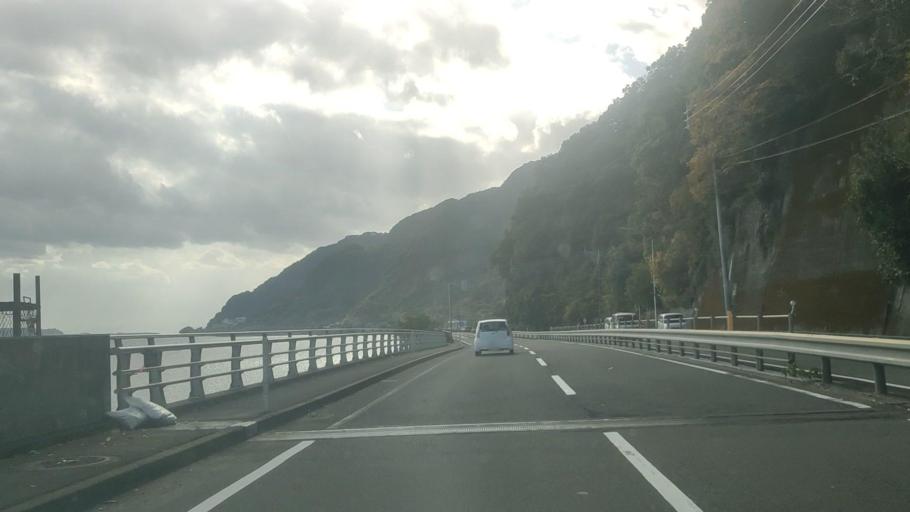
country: JP
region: Kagoshima
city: Kajiki
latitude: 31.6522
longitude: 130.6080
